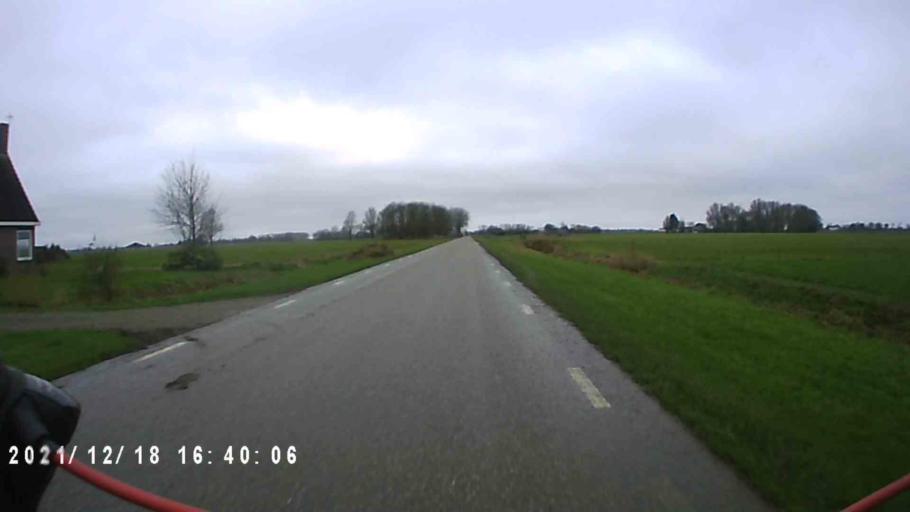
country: NL
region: Friesland
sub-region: Gemeente Dongeradeel
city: Dokkum
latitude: 53.3608
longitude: 6.0039
